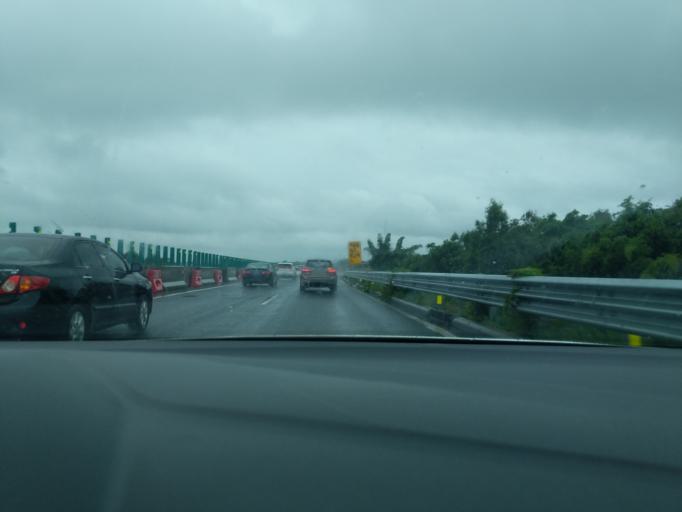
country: CN
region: Guangdong
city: Yueshan
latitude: 22.4648
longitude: 112.7052
